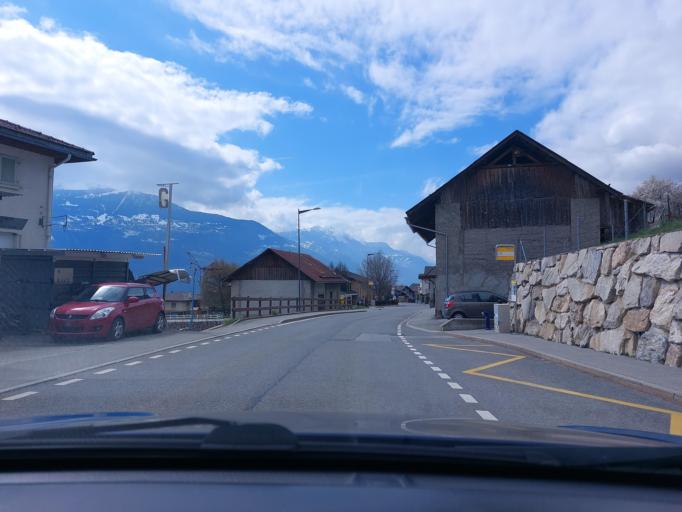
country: CH
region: Valais
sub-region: Conthey District
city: Conthey
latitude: 46.2404
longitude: 7.2954
